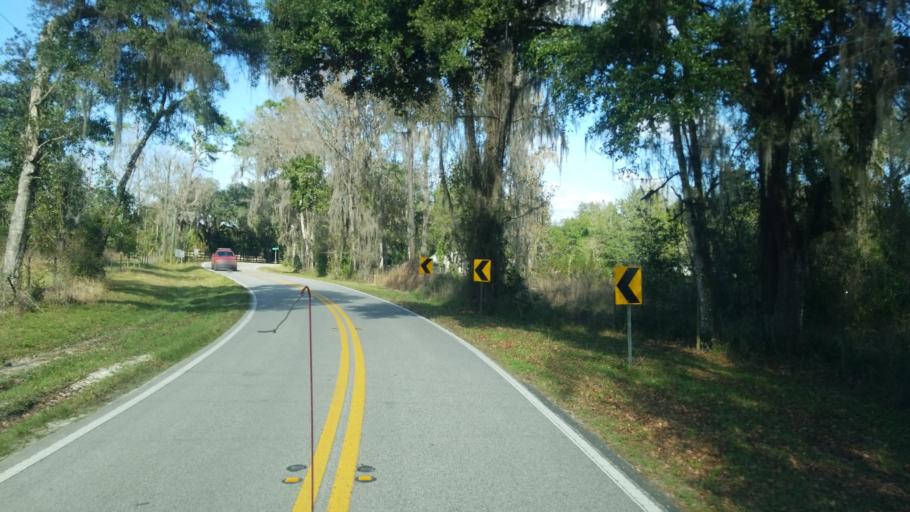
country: US
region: Florida
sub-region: Hernando County
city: North Brooksville
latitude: 28.6065
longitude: -82.3794
